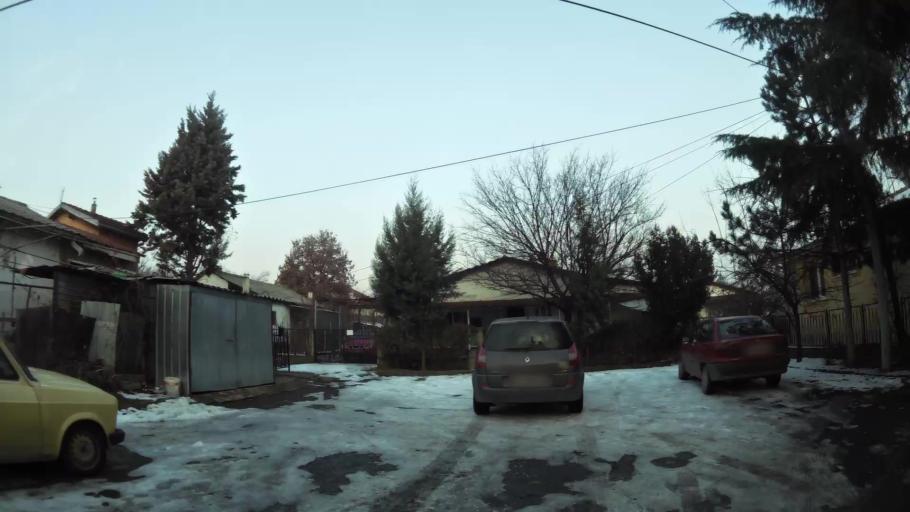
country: MK
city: Creshevo
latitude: 42.0096
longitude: 21.5062
